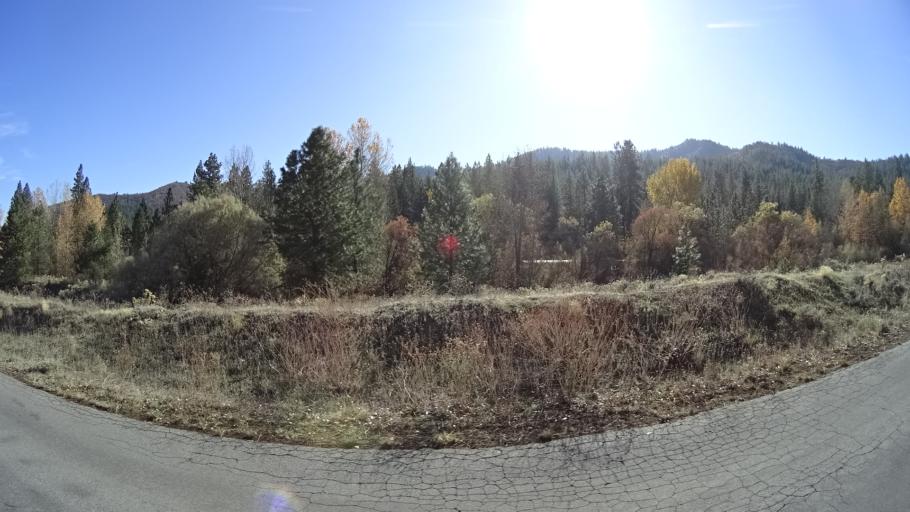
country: US
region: California
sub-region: Siskiyou County
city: Yreka
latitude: 41.7175
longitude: -122.6753
